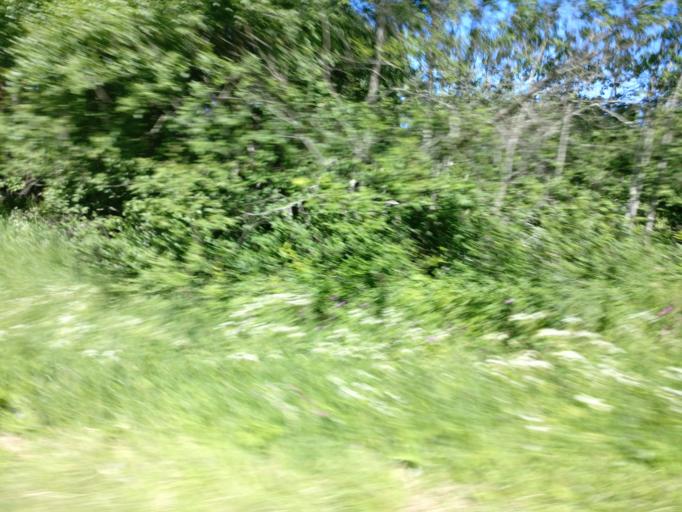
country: FI
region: Southern Savonia
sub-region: Savonlinna
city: Rantasalmi
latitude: 62.1007
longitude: 28.2624
